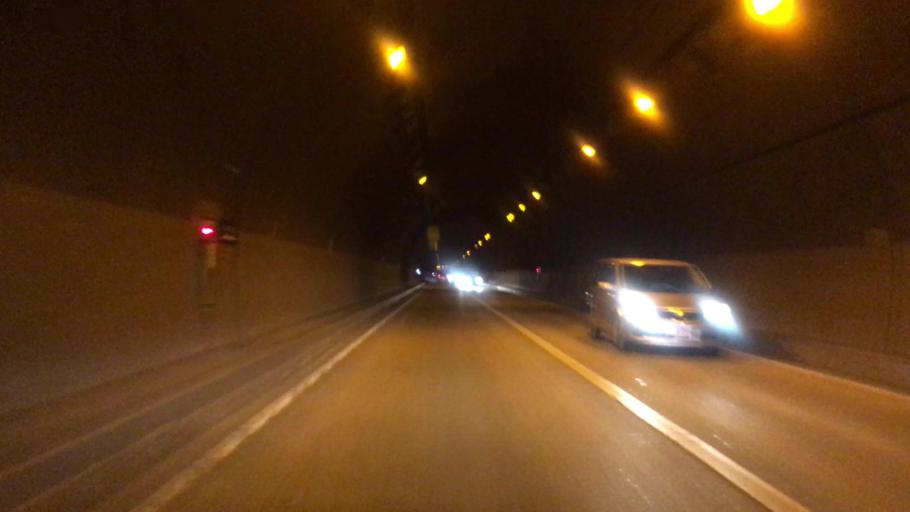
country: JP
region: Hyogo
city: Toyooka
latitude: 35.4753
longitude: 134.7754
